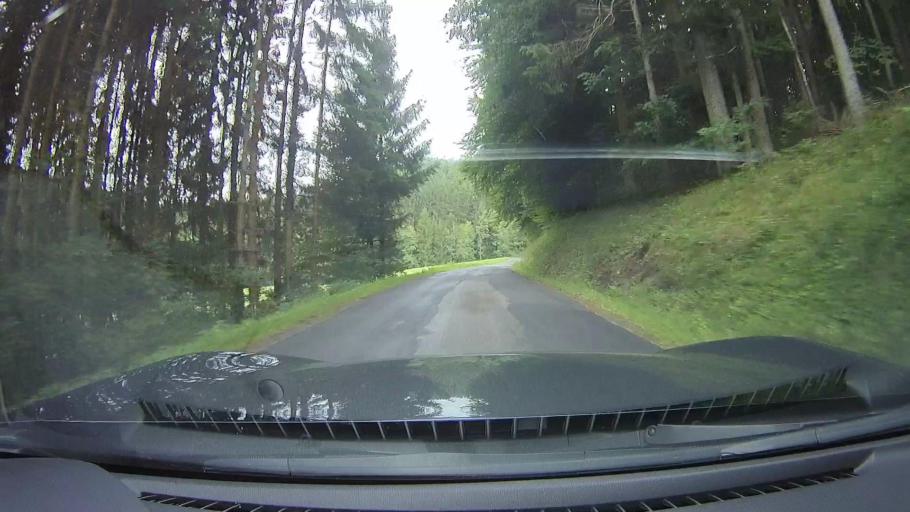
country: DE
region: Baden-Wuerttemberg
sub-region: Regierungsbezirk Stuttgart
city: Sulzbach an der Murr
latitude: 49.0046
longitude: 9.5365
